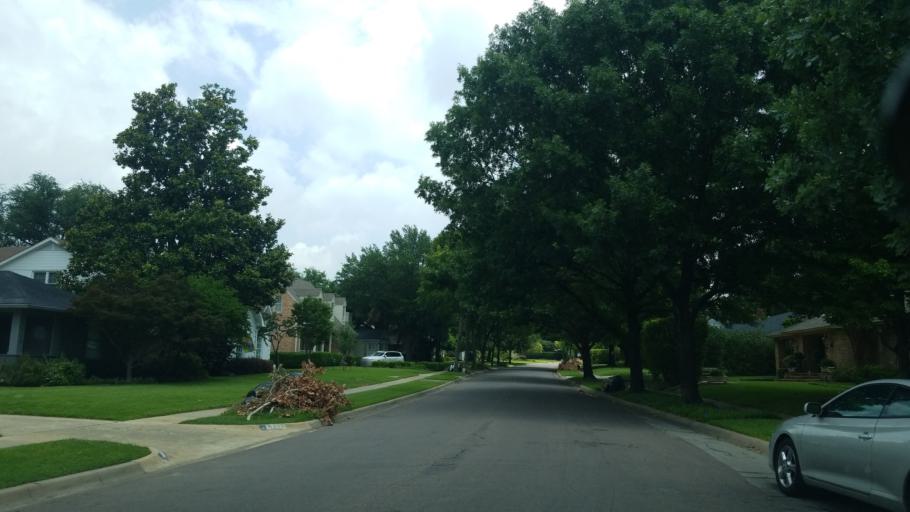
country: US
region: Texas
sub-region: Dallas County
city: University Park
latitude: 32.8347
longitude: -96.8216
